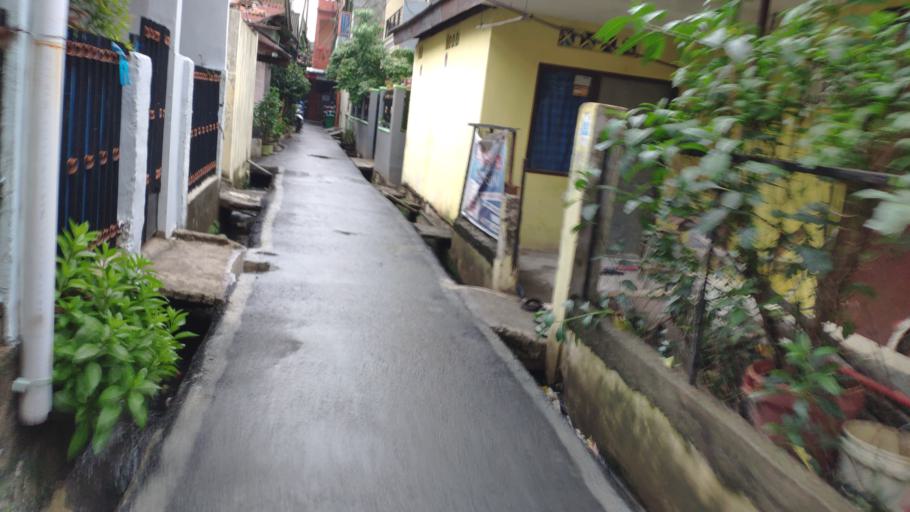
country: ID
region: Jakarta Raya
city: Jakarta
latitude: -6.2053
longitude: 106.8718
